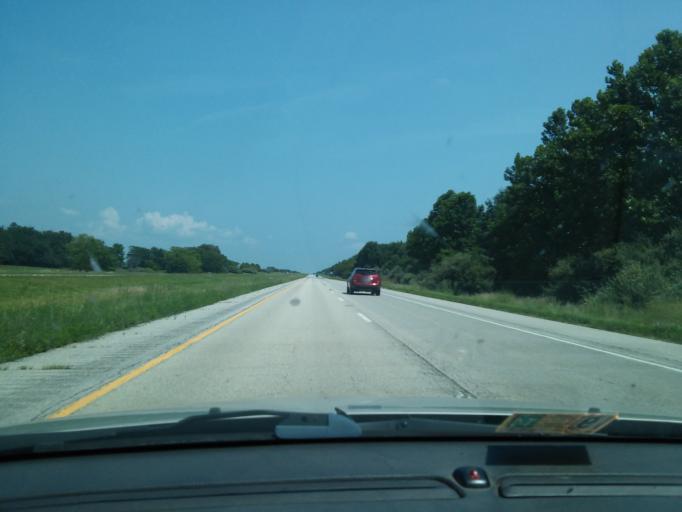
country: US
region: Illinois
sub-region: Sangamon County
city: New Berlin
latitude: 39.7398
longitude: -89.9609
